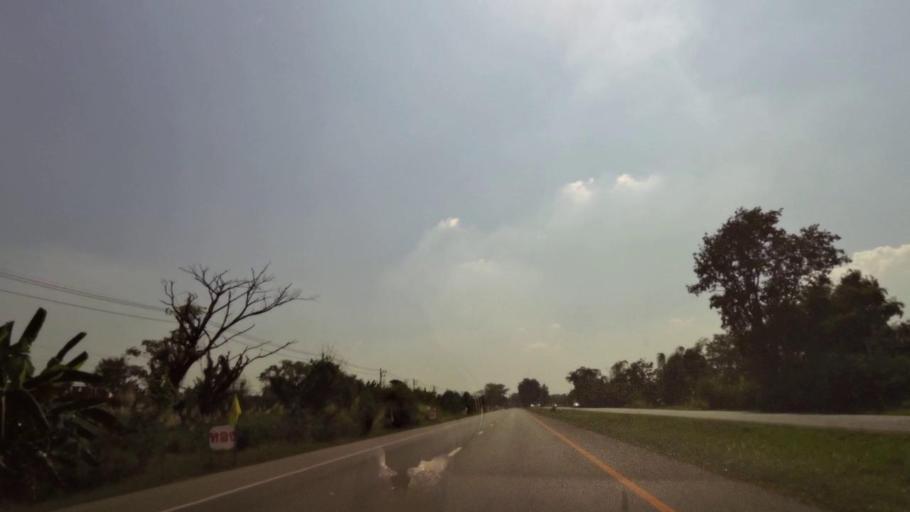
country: TH
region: Phichit
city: Bueng Na Rang
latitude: 16.2398
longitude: 100.1254
